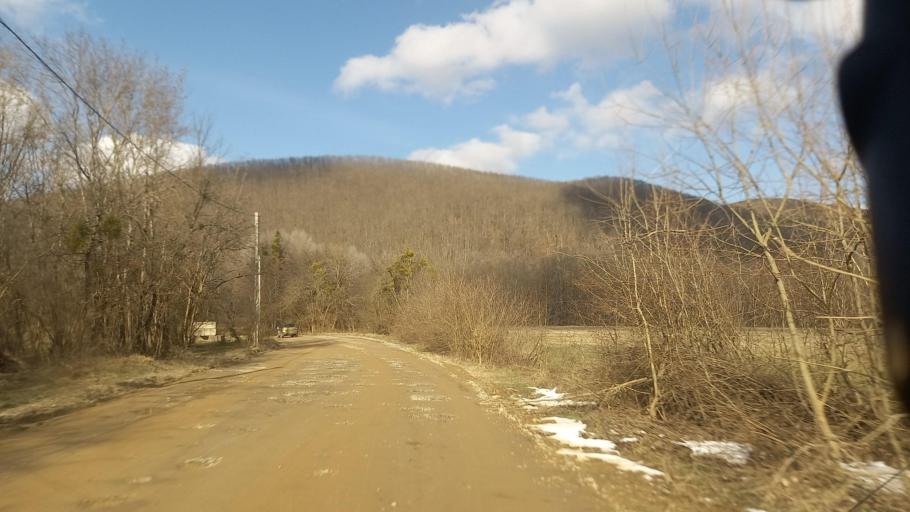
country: RU
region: Krasnodarskiy
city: Smolenskaya
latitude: 44.6024
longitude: 38.8435
